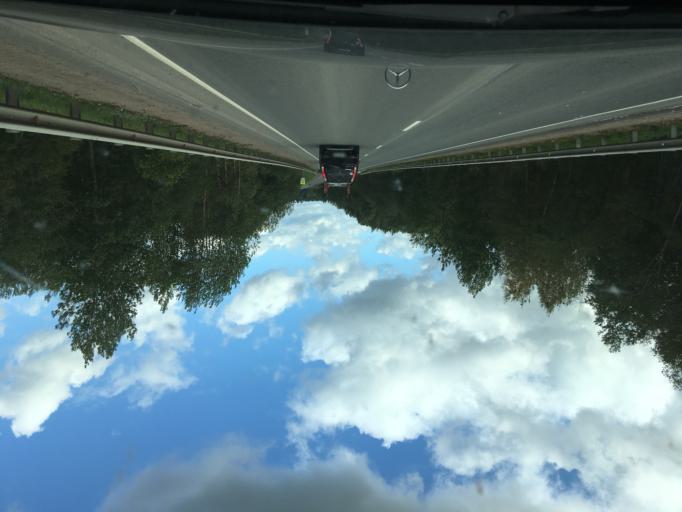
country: RU
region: Pskov
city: Novosokol'niki
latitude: 56.3016
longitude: 30.2125
